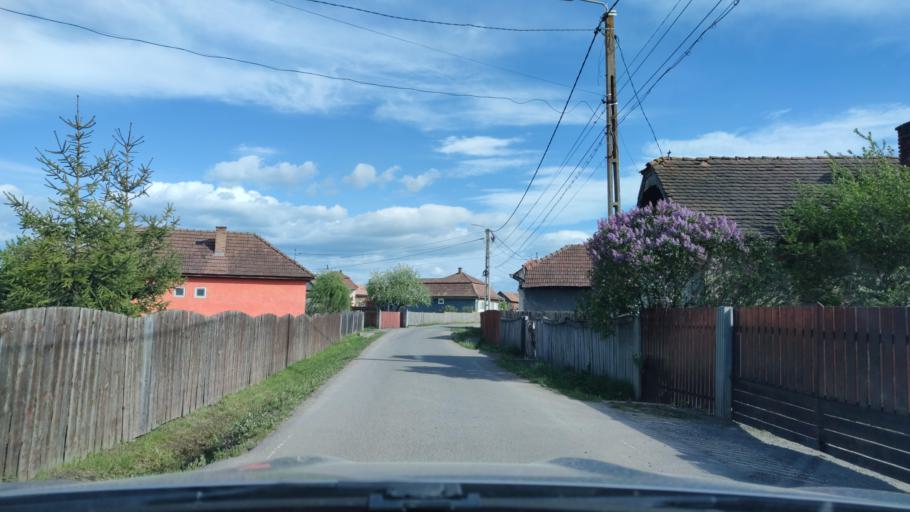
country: RO
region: Harghita
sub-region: Comuna Ditrau
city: Ditrau
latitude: 46.7965
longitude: 25.4874
